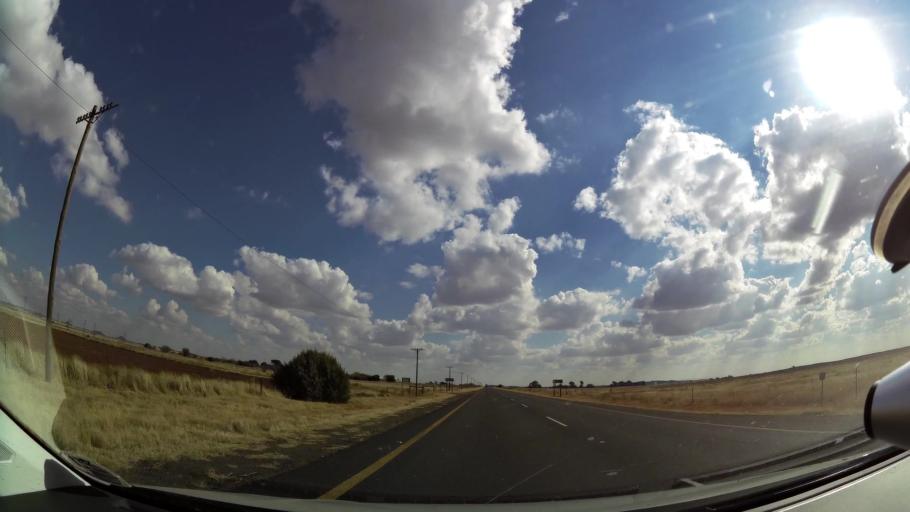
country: ZA
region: Orange Free State
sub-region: Xhariep District Municipality
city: Koffiefontein
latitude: -29.1278
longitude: 25.4872
